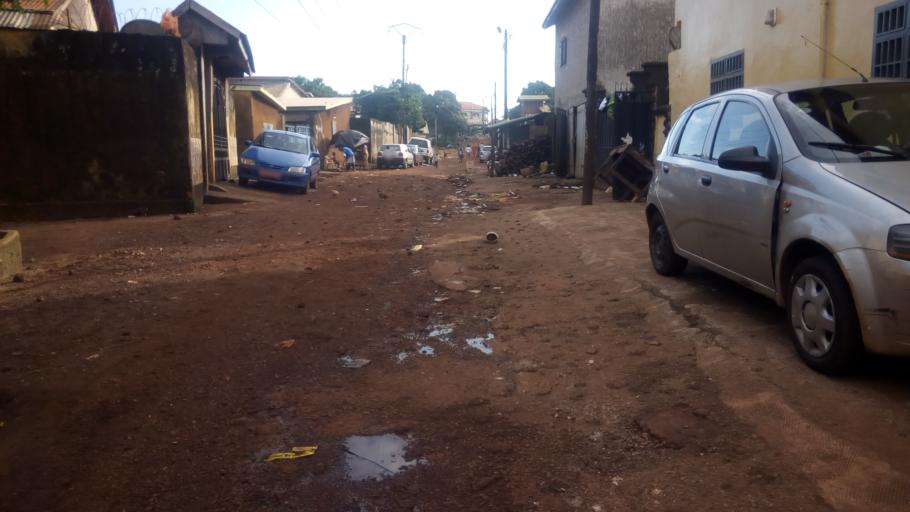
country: GN
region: Conakry
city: Conakry
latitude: 9.6247
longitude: -13.6106
